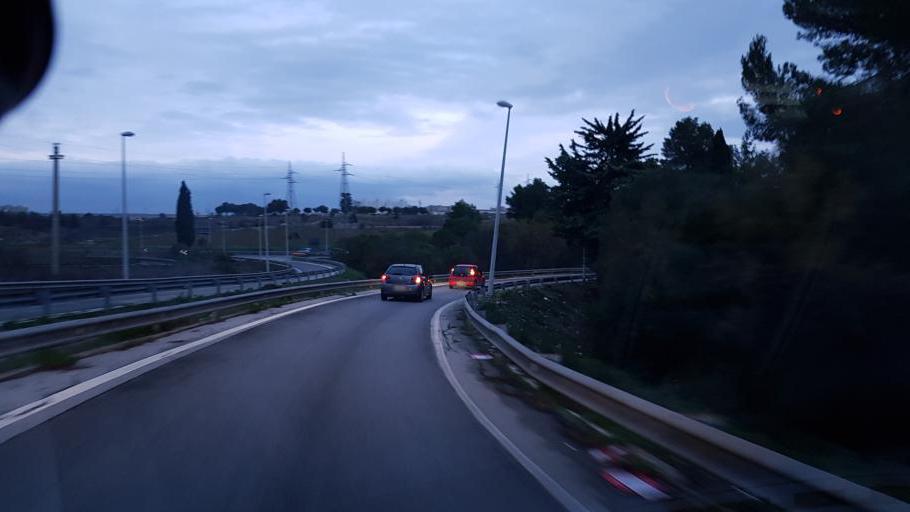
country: IT
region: Apulia
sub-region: Provincia di Taranto
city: Paolo VI
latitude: 40.5059
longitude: 17.2625
